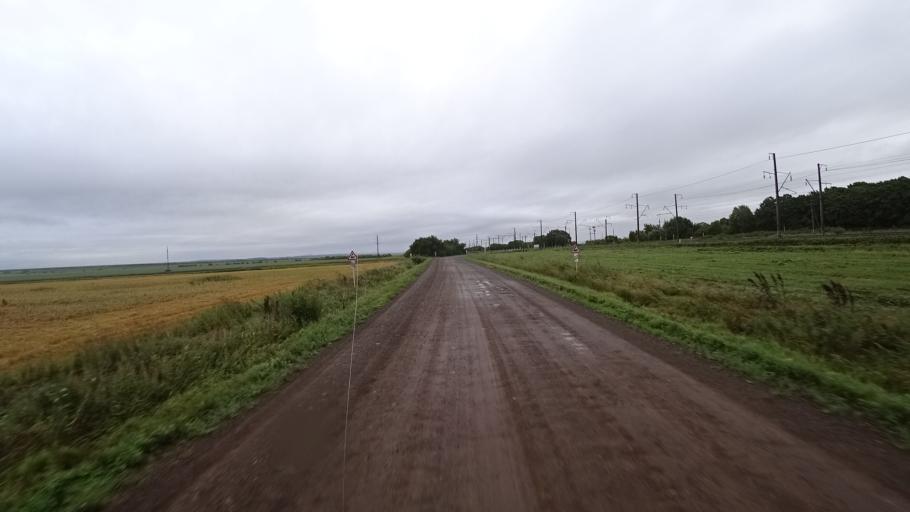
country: RU
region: Primorskiy
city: Monastyrishche
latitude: 44.2764
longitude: 132.4601
